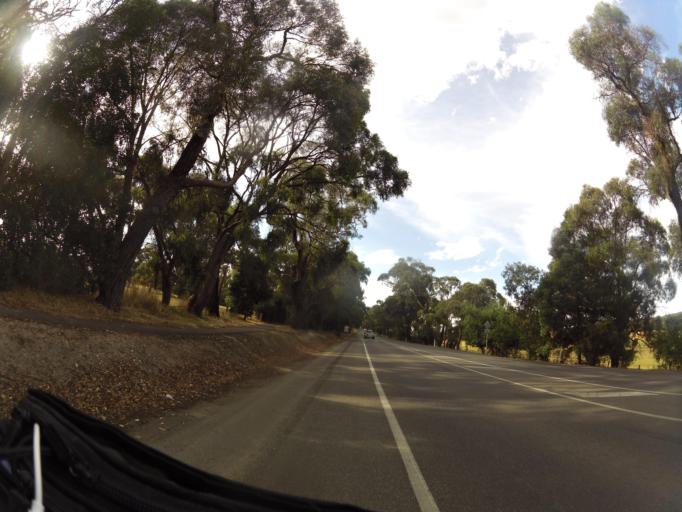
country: AU
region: Victoria
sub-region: Ballarat North
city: Mount Clear
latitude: -37.6175
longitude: 143.8746
